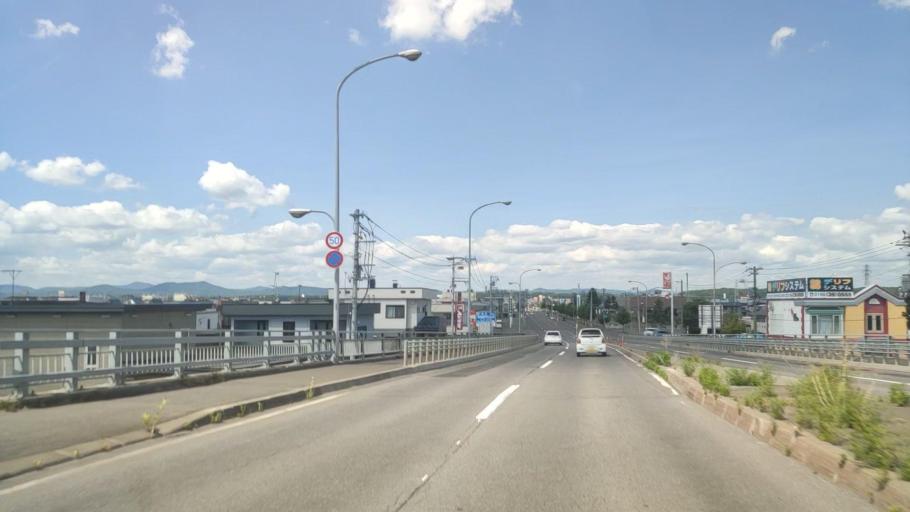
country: JP
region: Hokkaido
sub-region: Asahikawa-shi
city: Asahikawa
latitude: 43.7988
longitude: 142.3949
